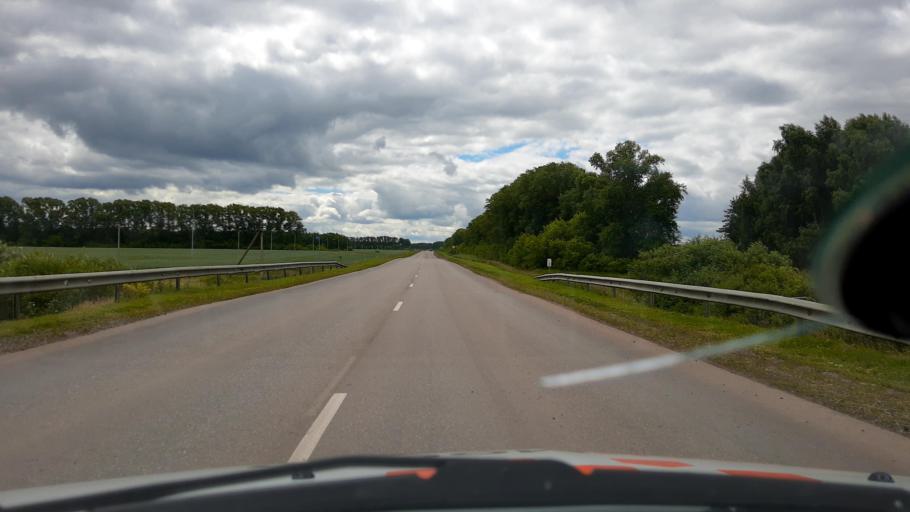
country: RU
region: Bashkortostan
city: Buzdyak
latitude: 54.6812
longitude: 54.5519
